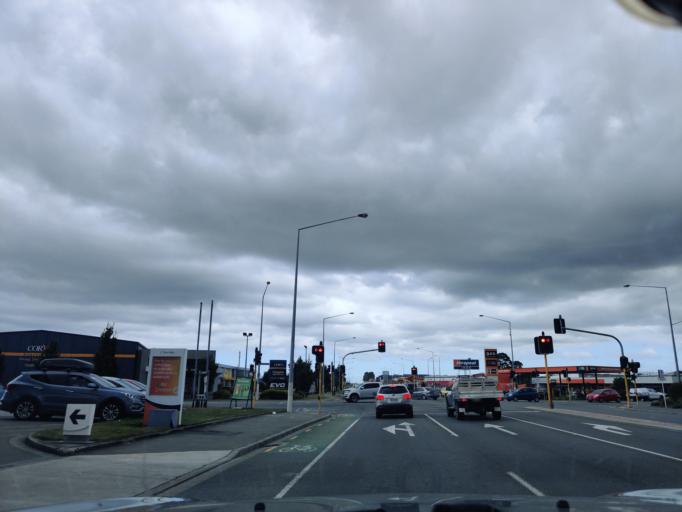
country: NZ
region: Canterbury
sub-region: Selwyn District
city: Prebbleton
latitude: -43.5380
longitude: 172.5283
